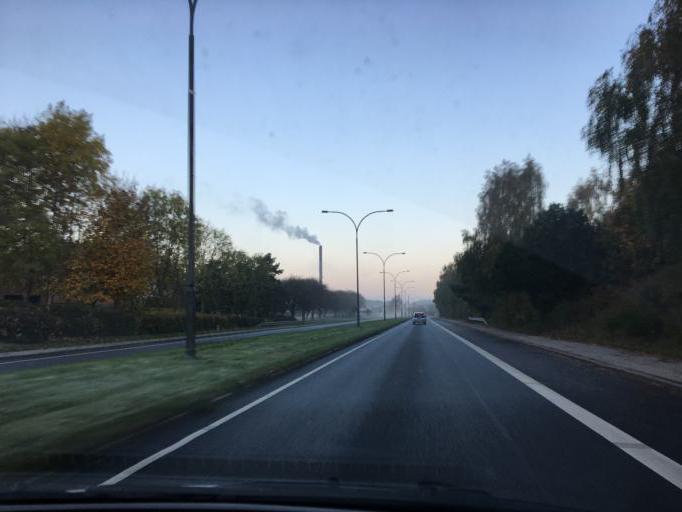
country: DK
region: South Denmark
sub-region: Vejle Kommune
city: Vejle
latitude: 55.6729
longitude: 9.5354
